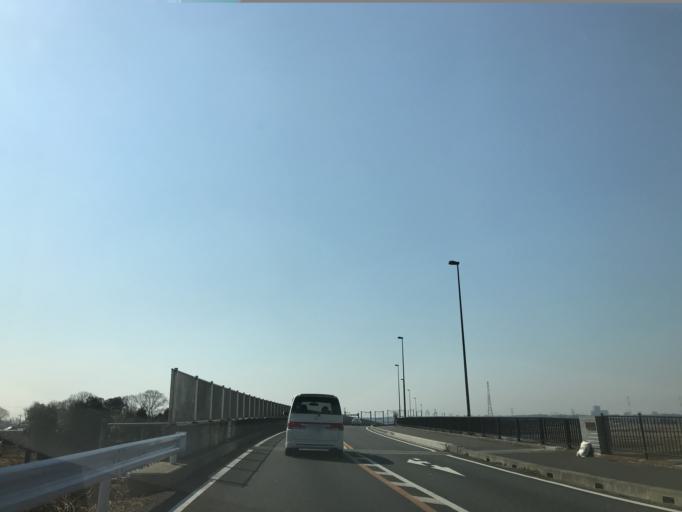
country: JP
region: Ibaraki
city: Mitsukaido
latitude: 35.9911
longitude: 140.0361
